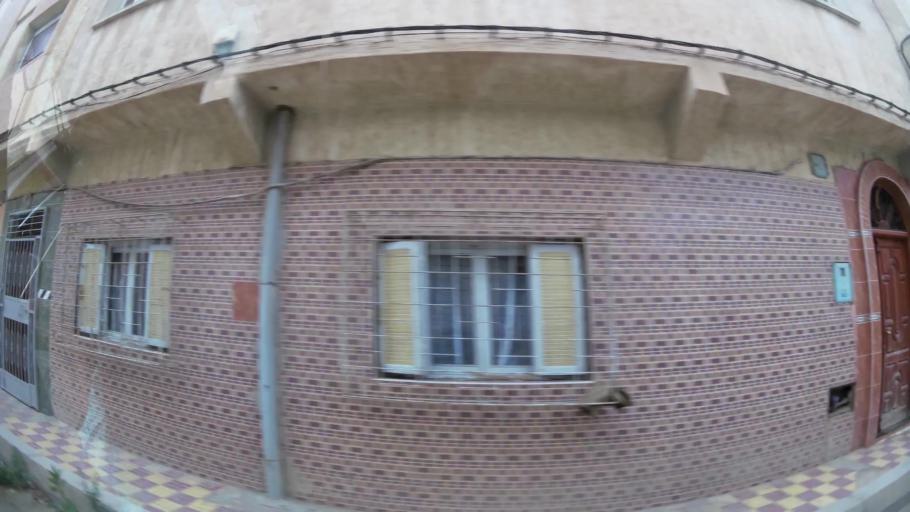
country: MA
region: Oriental
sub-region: Nador
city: Nador
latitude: 35.1622
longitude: -2.9403
